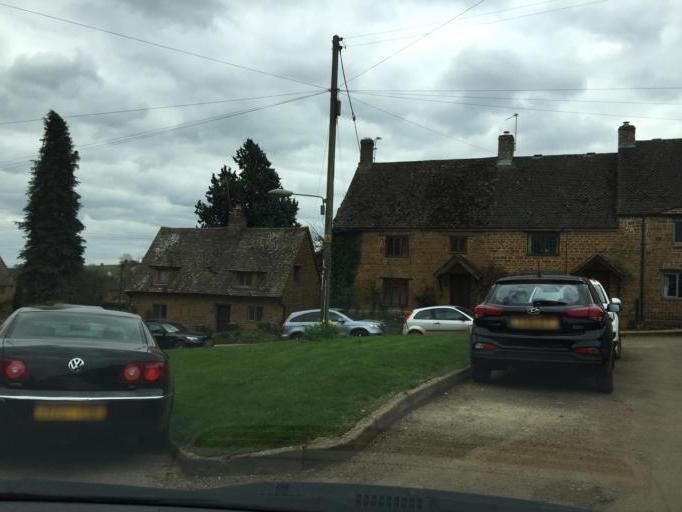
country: GB
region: England
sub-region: Oxfordshire
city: Hanwell
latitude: 52.1031
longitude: -1.4282
